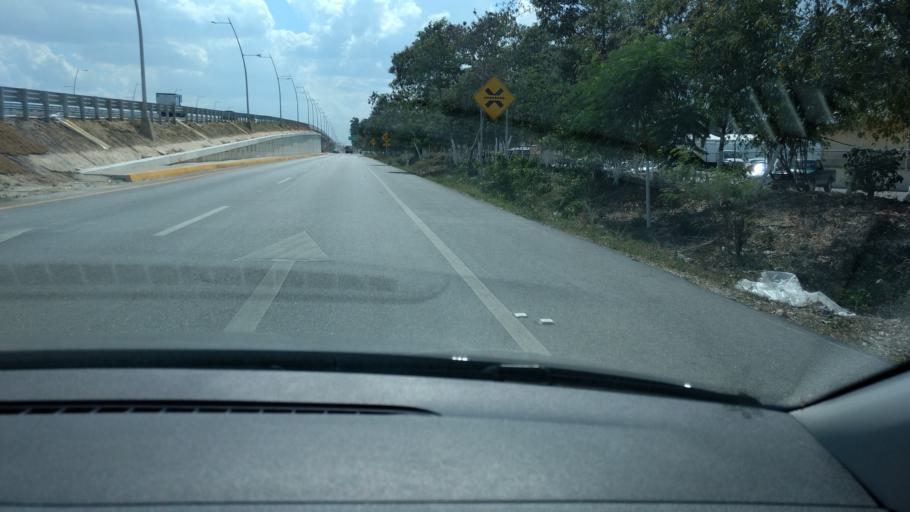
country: MX
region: Yucatan
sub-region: Kanasin
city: Kanasin
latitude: 20.9849
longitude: -89.5637
